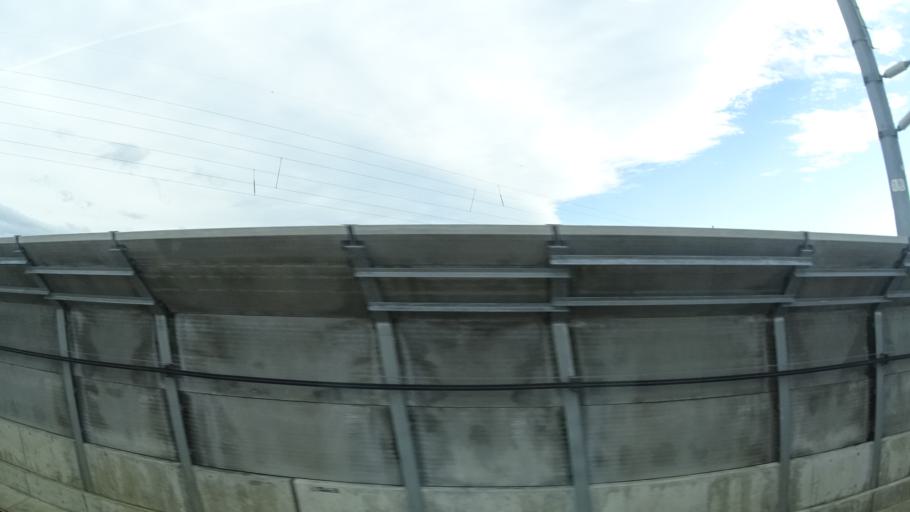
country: JP
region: Toyama
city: Kuragaki-kosugi
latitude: 36.7211
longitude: 137.1633
